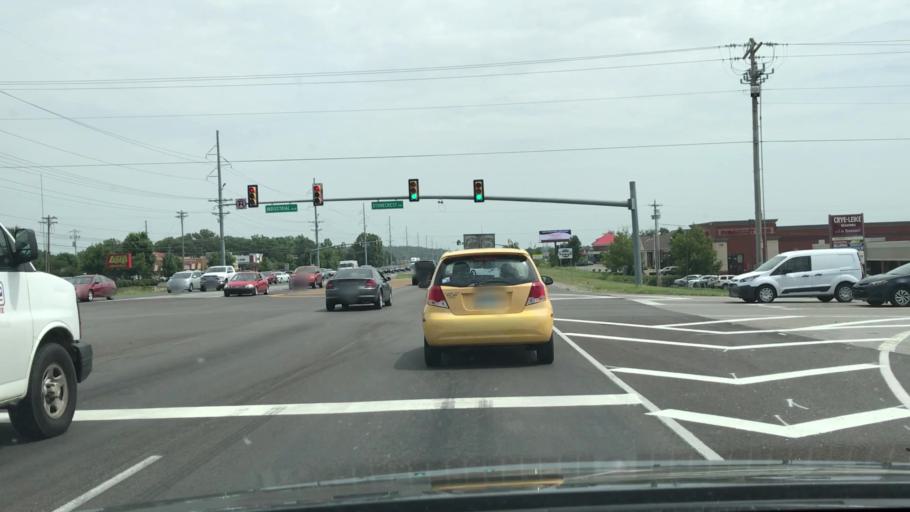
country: US
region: Tennessee
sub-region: Rutherford County
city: La Vergne
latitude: 35.9781
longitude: -86.5631
